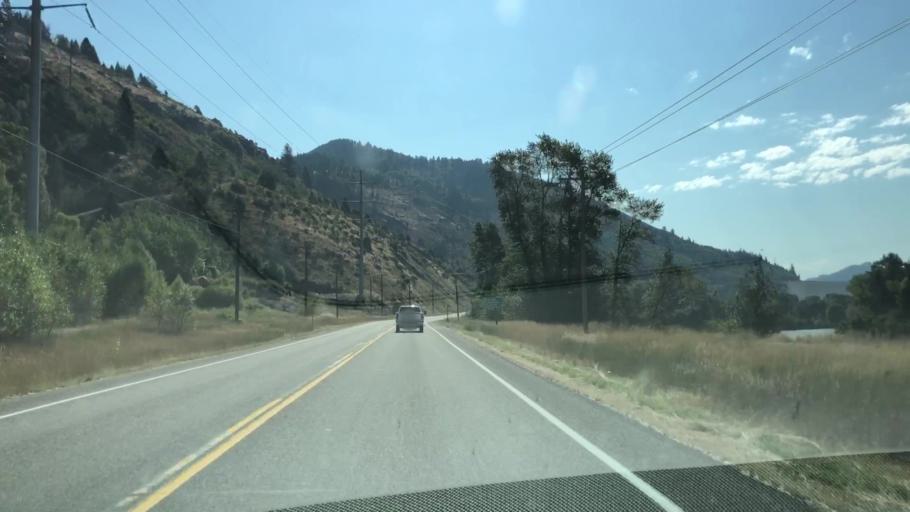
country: US
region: Idaho
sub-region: Teton County
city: Victor
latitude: 43.3476
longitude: -111.2114
